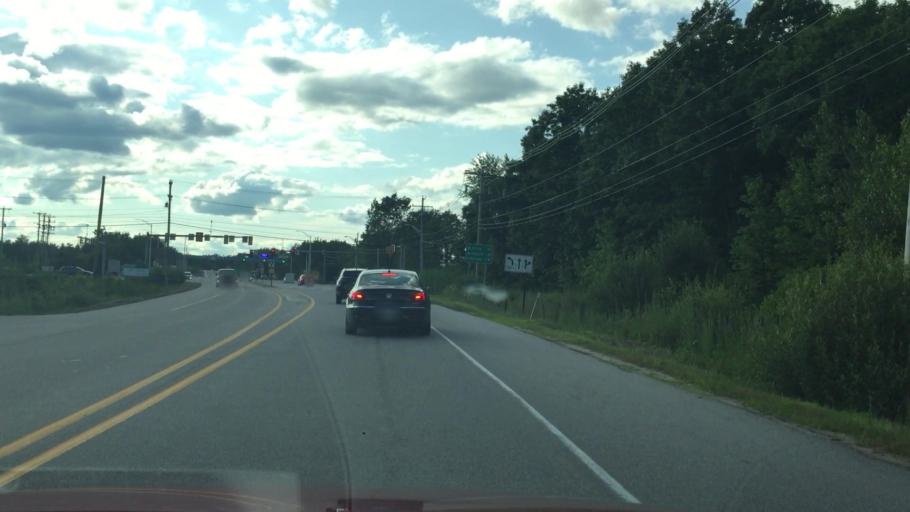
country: US
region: Maine
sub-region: Cumberland County
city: West Scarborough
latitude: 43.6024
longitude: -70.3648
